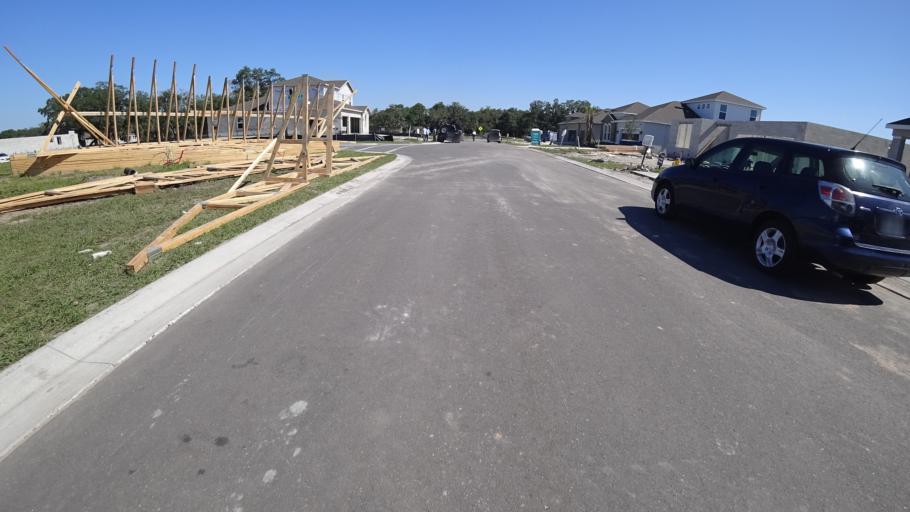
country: US
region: Florida
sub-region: Manatee County
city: Ellenton
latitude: 27.5710
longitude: -82.4437
